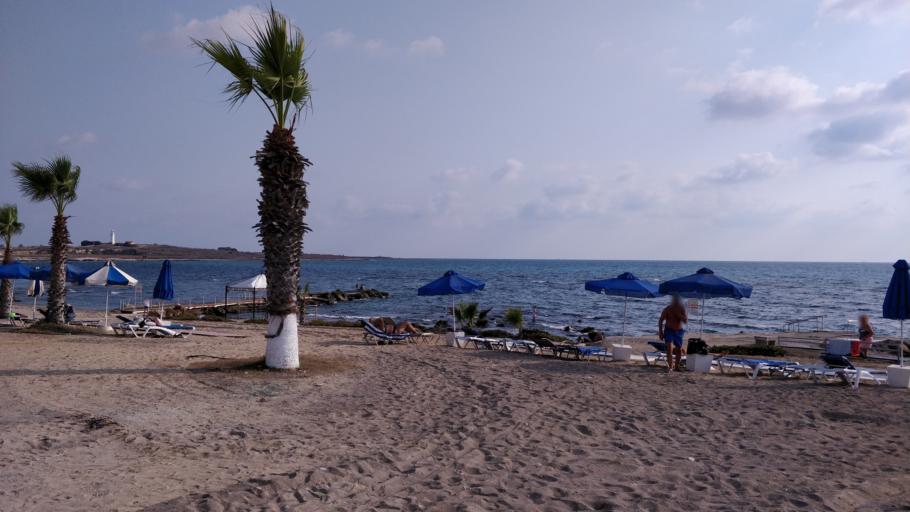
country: CY
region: Pafos
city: Paphos
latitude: 34.7700
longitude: 32.4048
